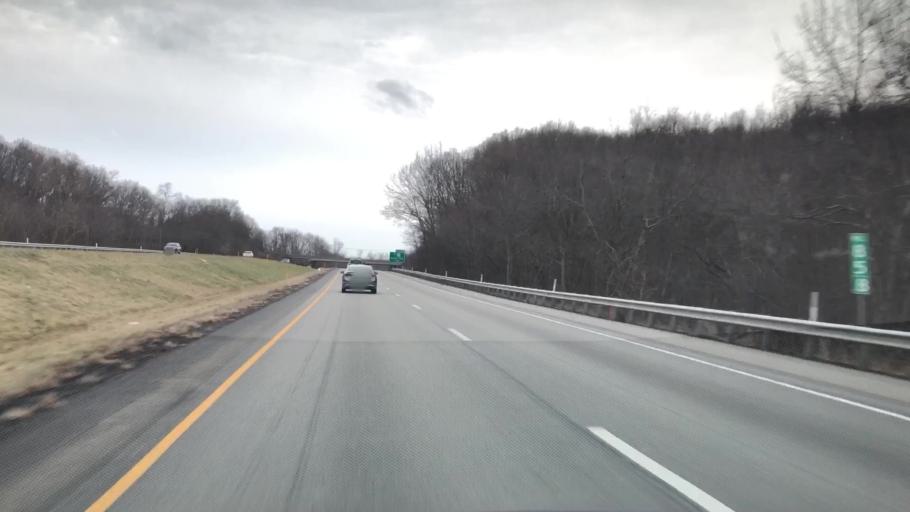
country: US
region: Pennsylvania
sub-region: Butler County
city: Zelienople
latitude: 40.7887
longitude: -80.1247
